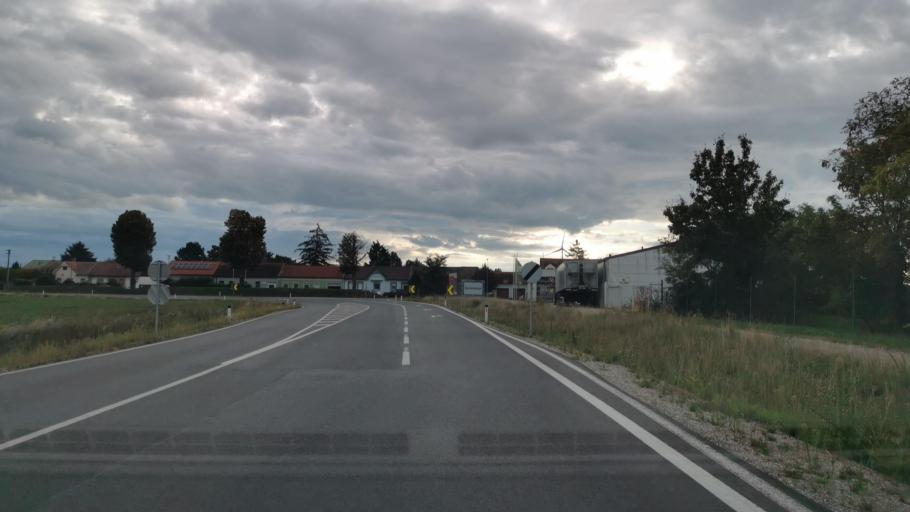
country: AT
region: Lower Austria
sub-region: Politischer Bezirk Ganserndorf
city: Obersiebenbrunn
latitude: 48.2467
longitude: 16.6987
